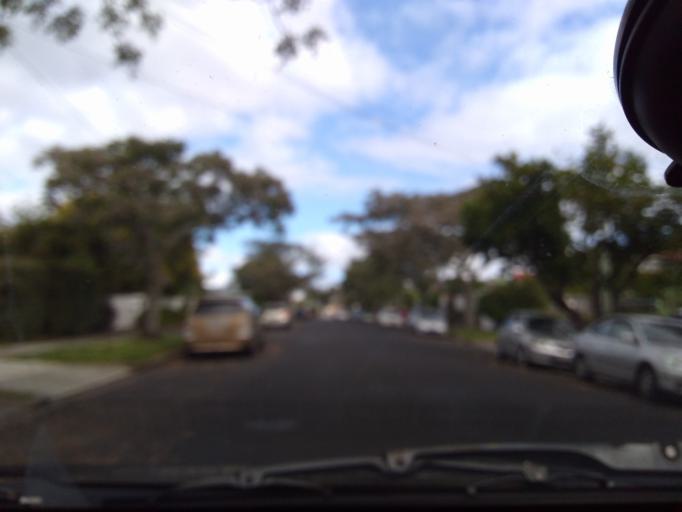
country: NZ
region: Auckland
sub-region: Auckland
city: Rosebank
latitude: -36.8760
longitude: 174.7175
